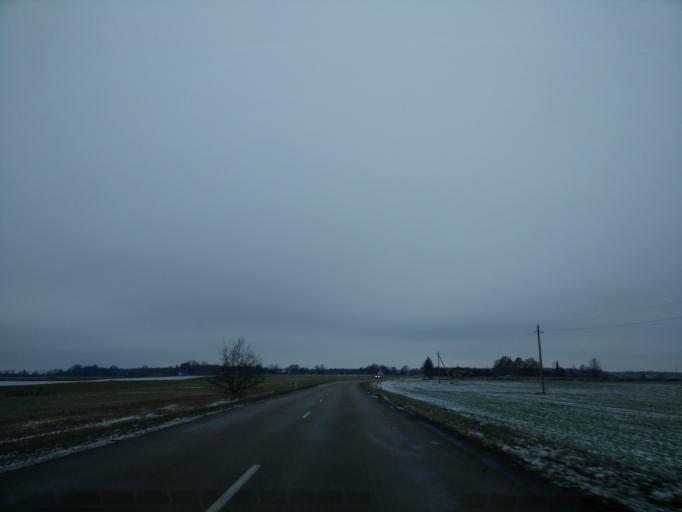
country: LT
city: Ariogala
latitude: 55.3799
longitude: 23.3498
